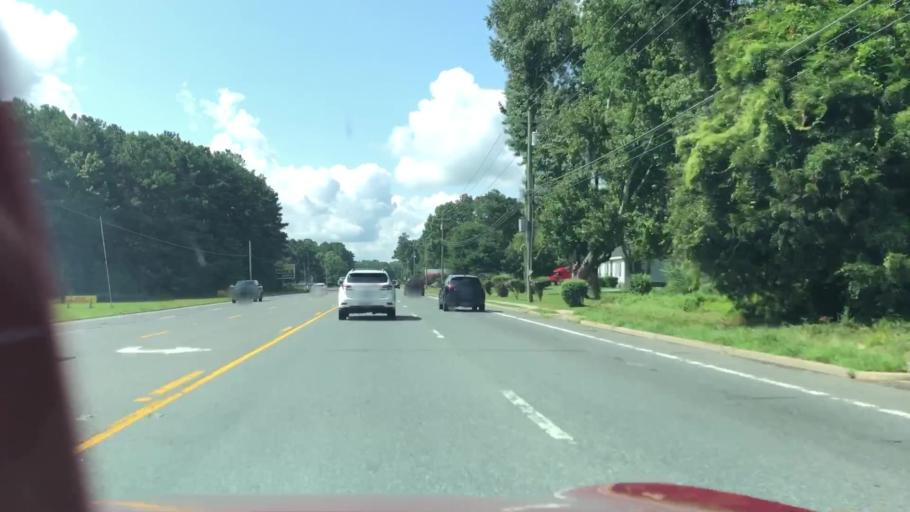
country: US
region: Virginia
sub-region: Accomack County
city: Wattsville
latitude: 37.8441
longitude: -75.5685
